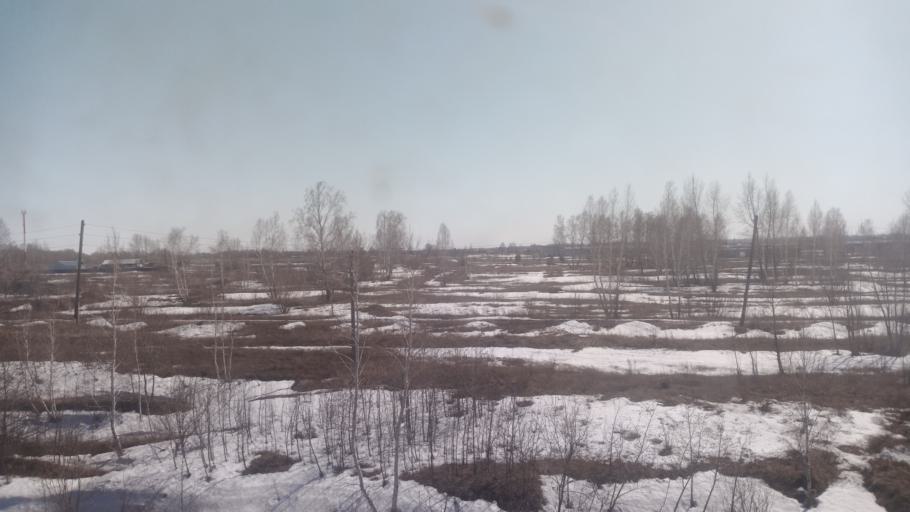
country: RU
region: Altai Krai
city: Beloyarsk
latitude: 53.4480
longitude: 83.9687
